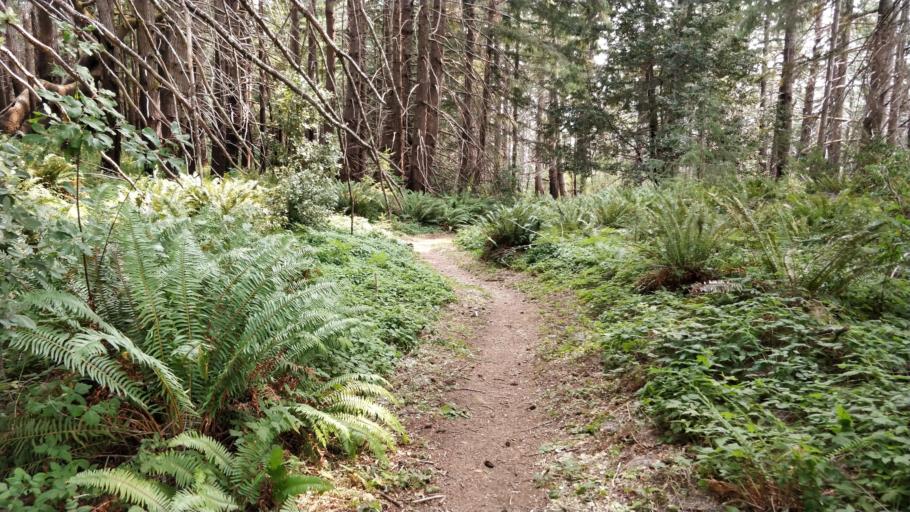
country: US
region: California
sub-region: Humboldt County
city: Westhaven-Moonstone
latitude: 41.2043
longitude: -123.9501
